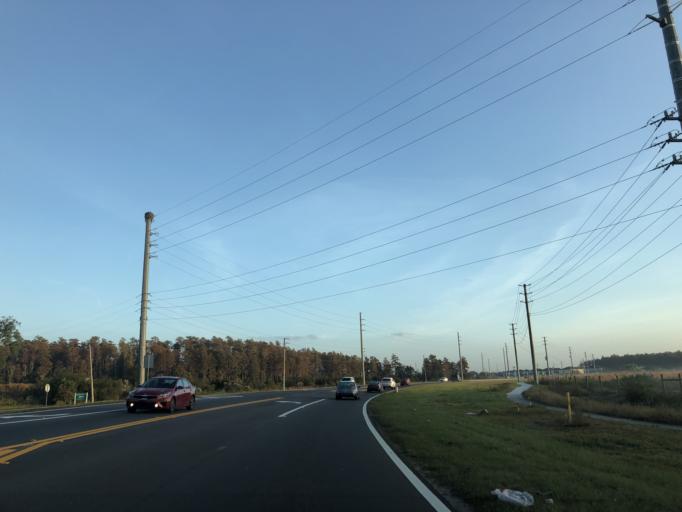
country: US
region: Florida
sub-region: Osceola County
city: Kissimmee
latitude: 28.3168
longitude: -81.4450
